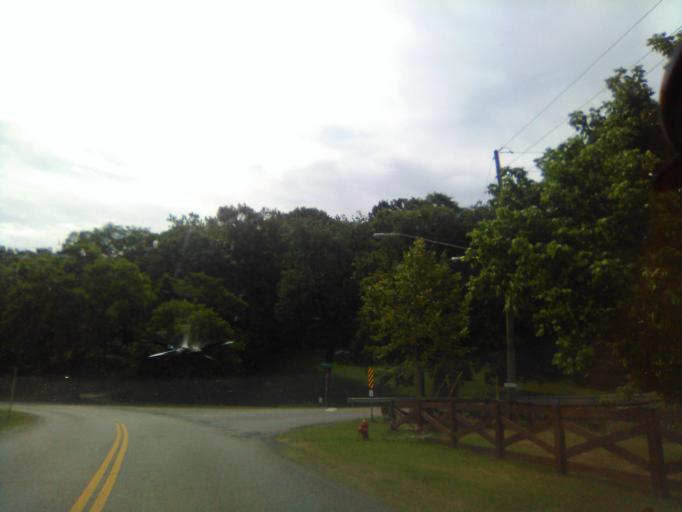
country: US
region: Tennessee
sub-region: Davidson County
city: Belle Meade
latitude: 36.1022
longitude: -86.8945
